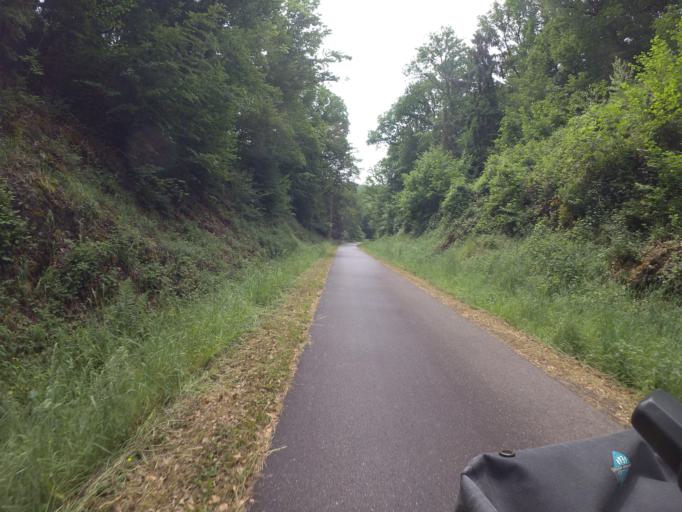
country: DE
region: Rheinland-Pfalz
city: Wittlich
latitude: 50.0081
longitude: 6.8887
